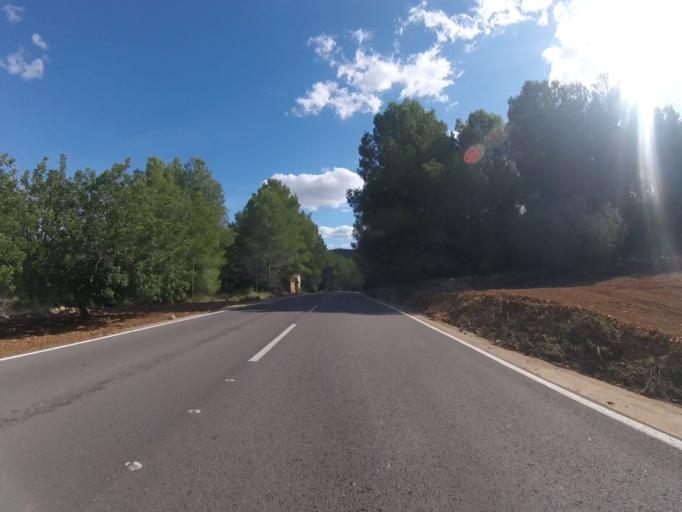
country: ES
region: Valencia
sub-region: Provincia de Castello
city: Cuevas de Vinroma
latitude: 40.3044
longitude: 0.1637
